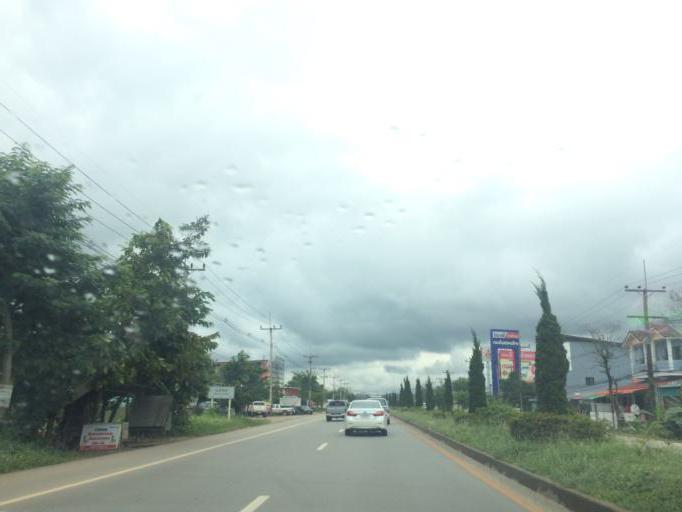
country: TH
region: Chiang Rai
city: Chiang Rai
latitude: 20.0197
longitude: 99.8707
